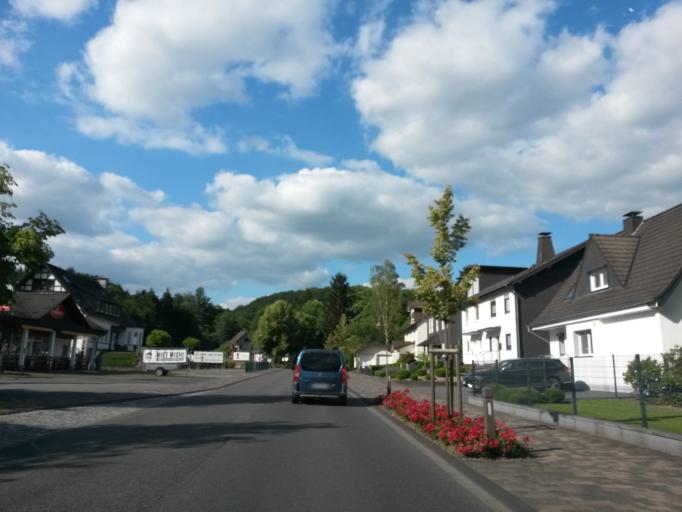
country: DE
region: North Rhine-Westphalia
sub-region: Regierungsbezirk Koln
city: Ruppichteroth
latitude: 50.8391
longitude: 7.4386
